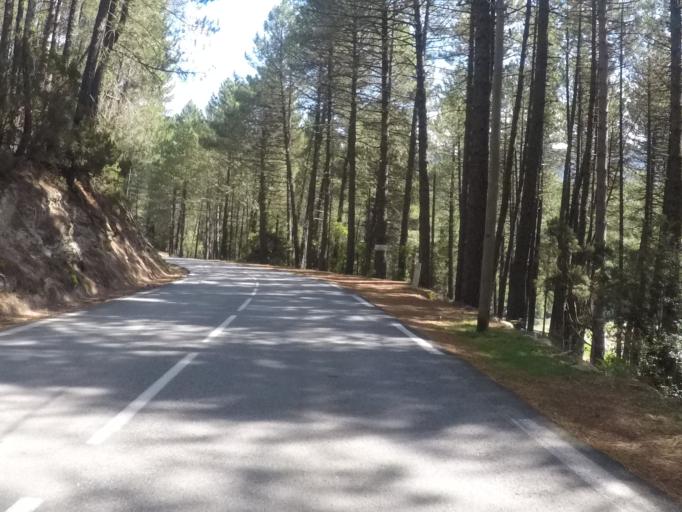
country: FR
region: Corsica
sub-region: Departement de la Corse-du-Sud
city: Zonza
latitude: 41.7653
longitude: 9.2008
